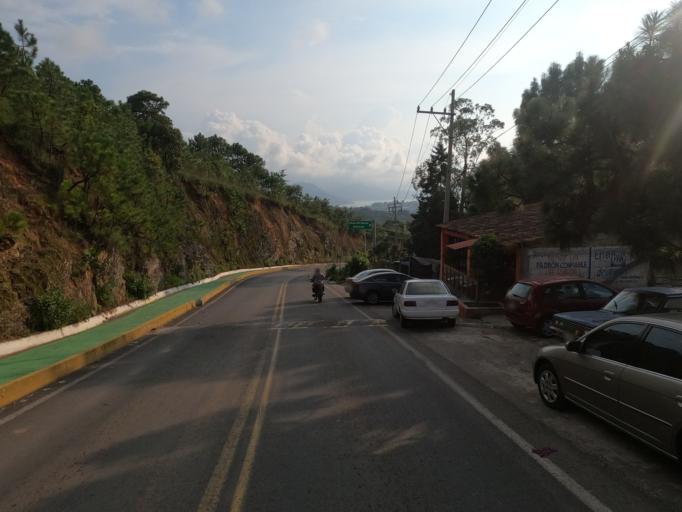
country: MX
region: Mexico
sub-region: Valle de Bravo
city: Colonia Rincon Villa del Valle
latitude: 19.2070
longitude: -100.1147
